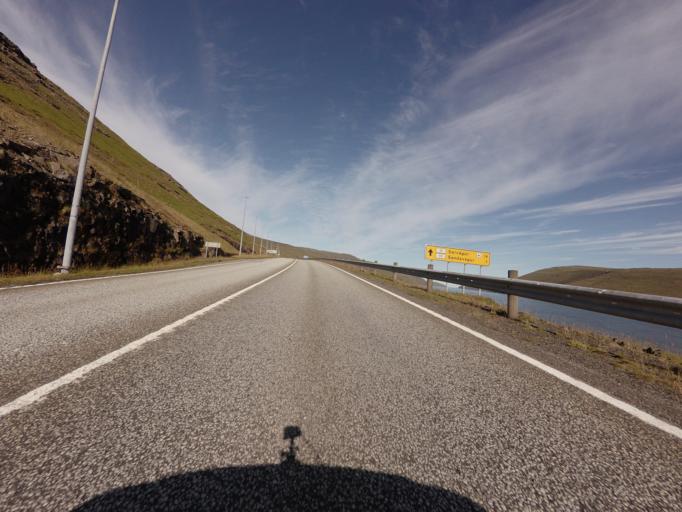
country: FO
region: Streymoy
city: Vestmanna
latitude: 62.0996
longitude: -7.1191
